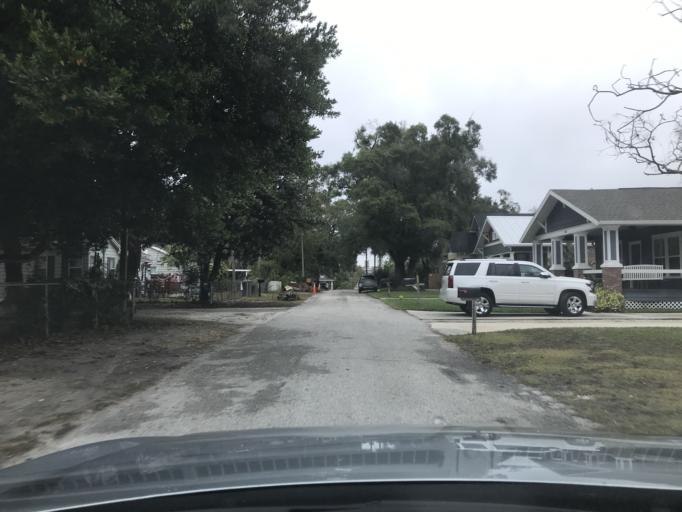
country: US
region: Florida
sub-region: Hillsborough County
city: Tampa
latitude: 27.9839
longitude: -82.4563
